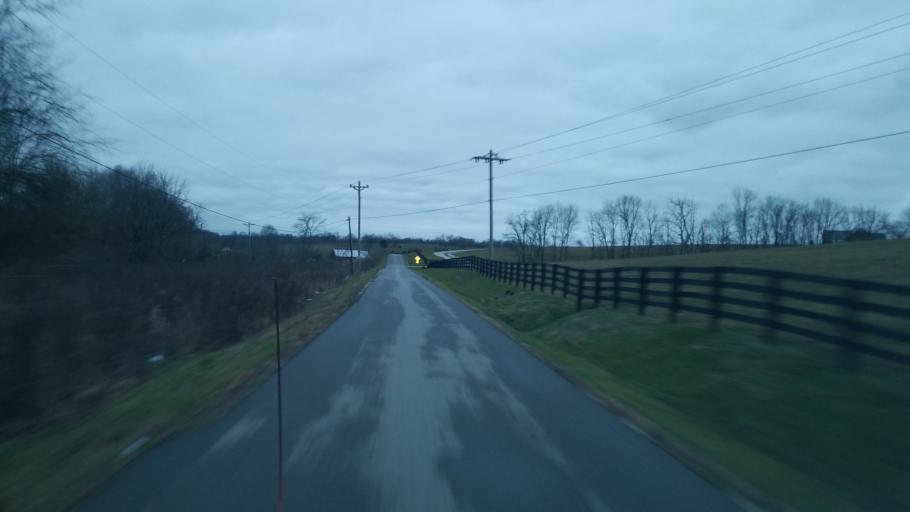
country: US
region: Kentucky
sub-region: Fleming County
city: Flemingsburg
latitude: 38.5039
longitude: -83.6951
